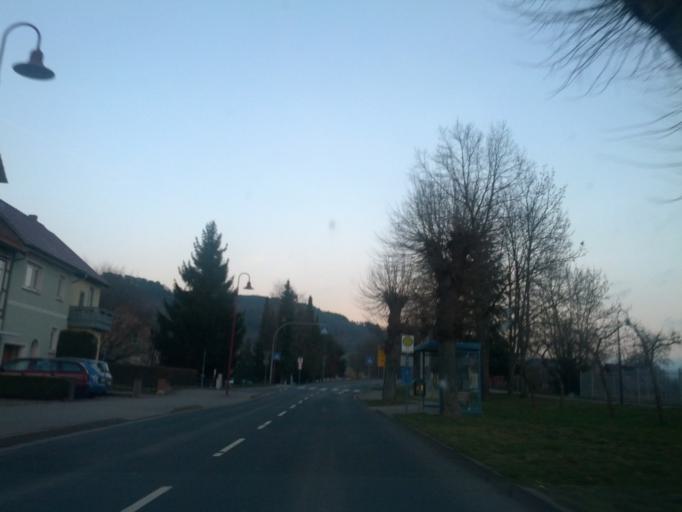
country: DE
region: Thuringia
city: Treffurt
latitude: 51.1352
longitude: 10.2348
